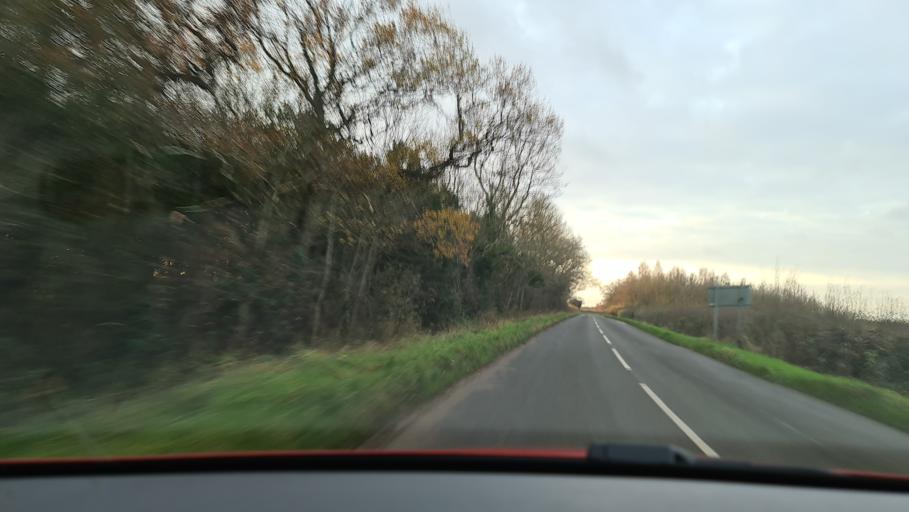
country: GB
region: England
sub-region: Oxfordshire
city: Somerton
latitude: 51.8909
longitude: -1.2731
